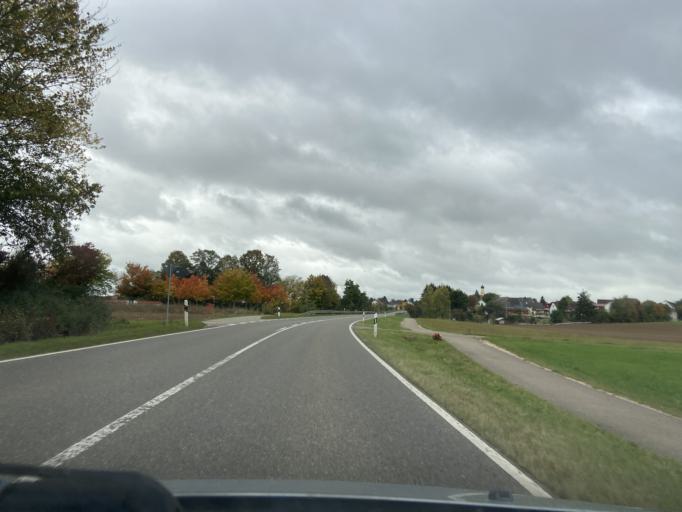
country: DE
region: Baden-Wuerttemberg
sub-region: Tuebingen Region
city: Inzigkofen
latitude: 48.0487
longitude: 9.1398
